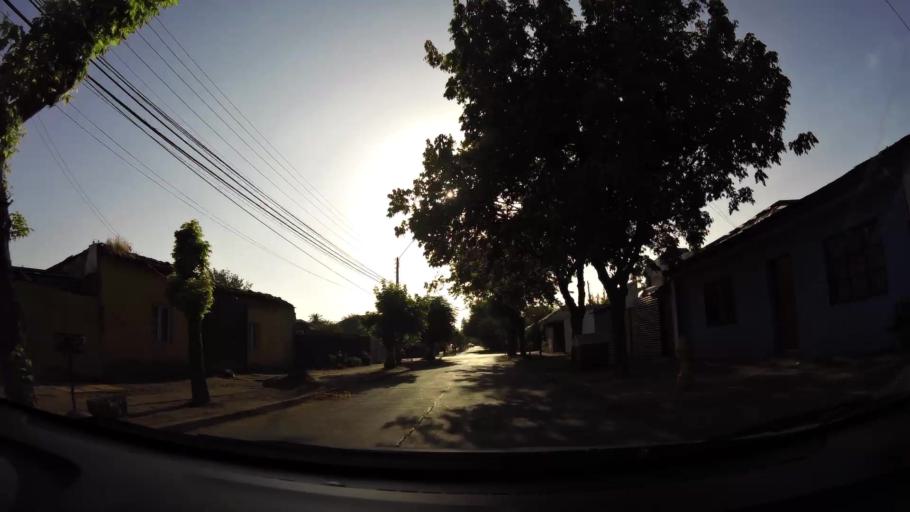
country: CL
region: Maule
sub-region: Provincia de Talca
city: Talca
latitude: -35.4132
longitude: -71.6593
